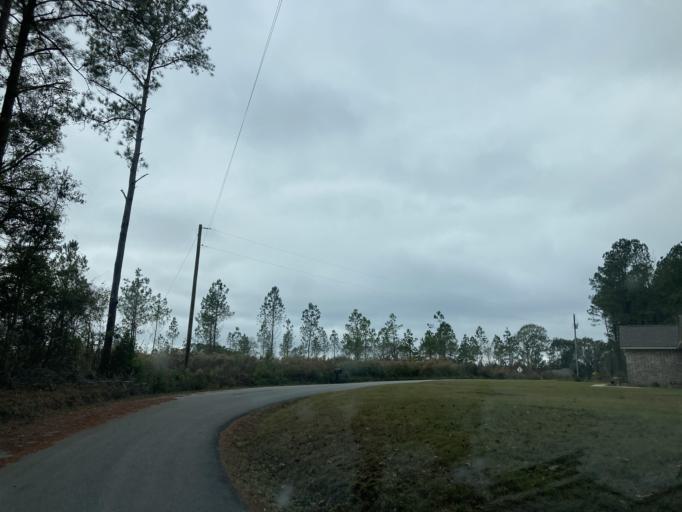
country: US
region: Mississippi
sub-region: Lamar County
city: Purvis
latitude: 31.1896
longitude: -89.4244
